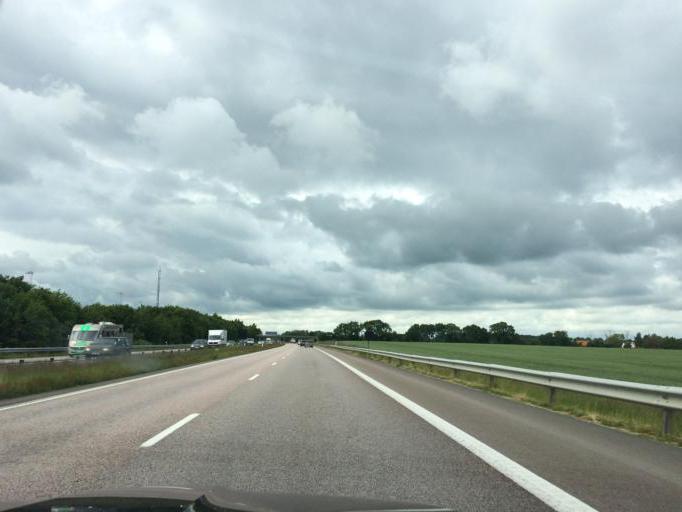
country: SE
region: Skane
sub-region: Helsingborg
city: Barslov
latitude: 56.0374
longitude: 12.7864
